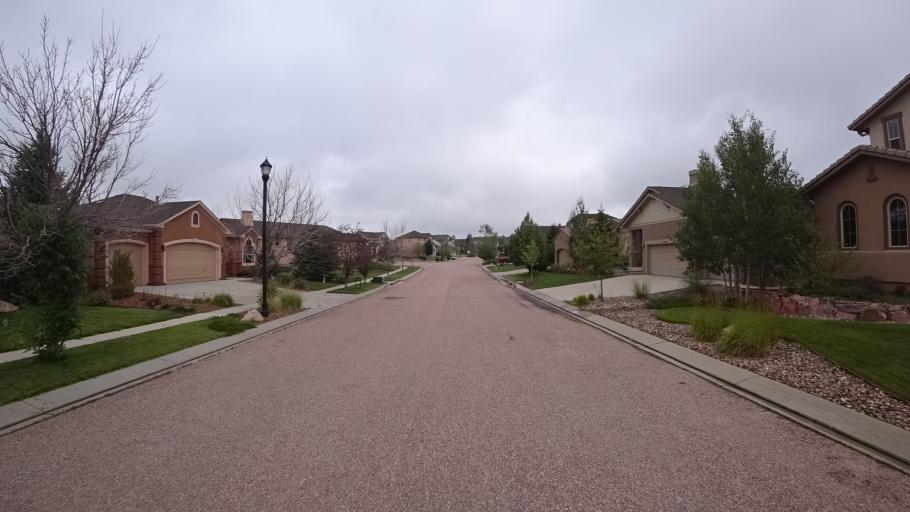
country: US
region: Colorado
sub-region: El Paso County
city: Gleneagle
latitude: 39.0315
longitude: -104.7802
